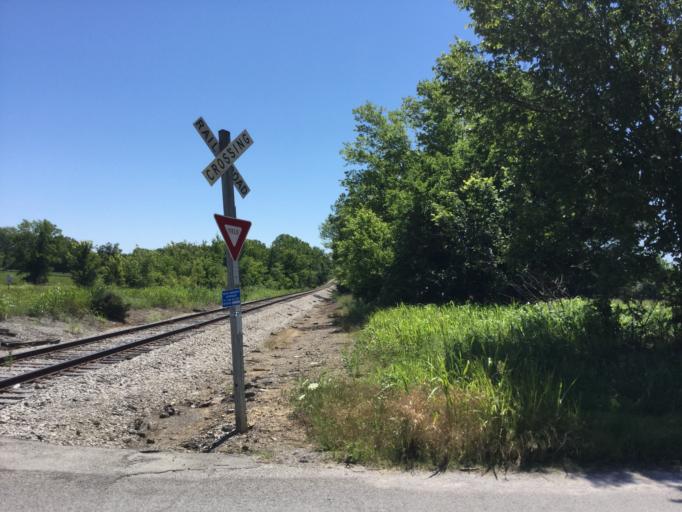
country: US
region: Kansas
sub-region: Montgomery County
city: Cherryvale
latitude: 37.2665
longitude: -95.5180
